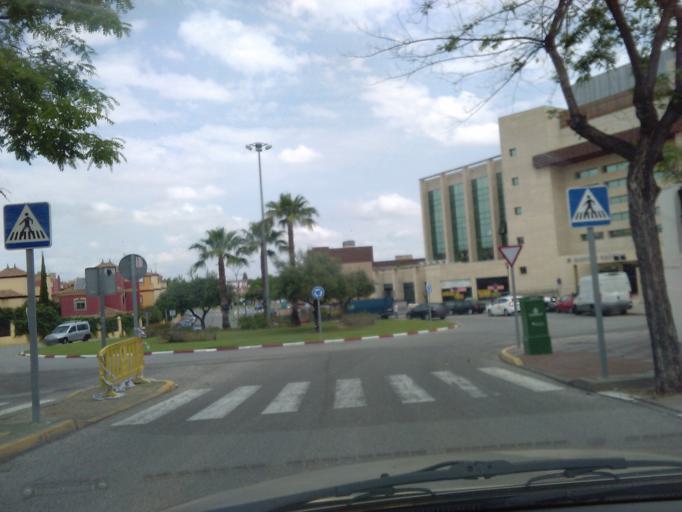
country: ES
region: Andalusia
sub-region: Provincia de Sevilla
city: Tomares
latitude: 37.3673
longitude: -6.0416
